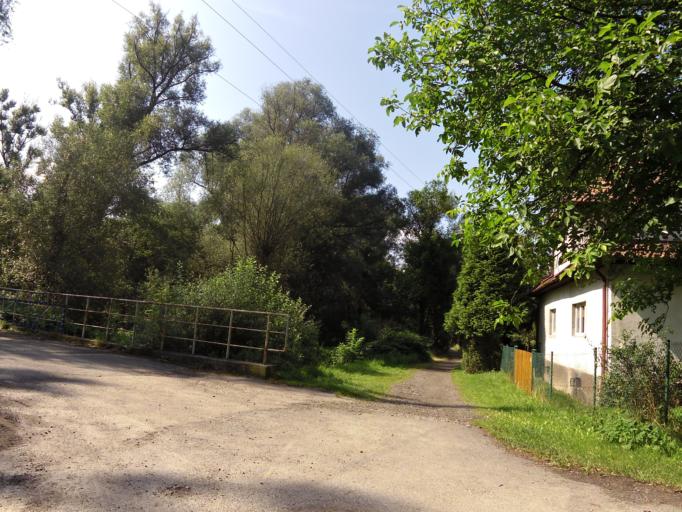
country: PL
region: Silesian Voivodeship
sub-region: Powiat zywiecki
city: Wieprz
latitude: 49.6552
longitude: 19.1822
